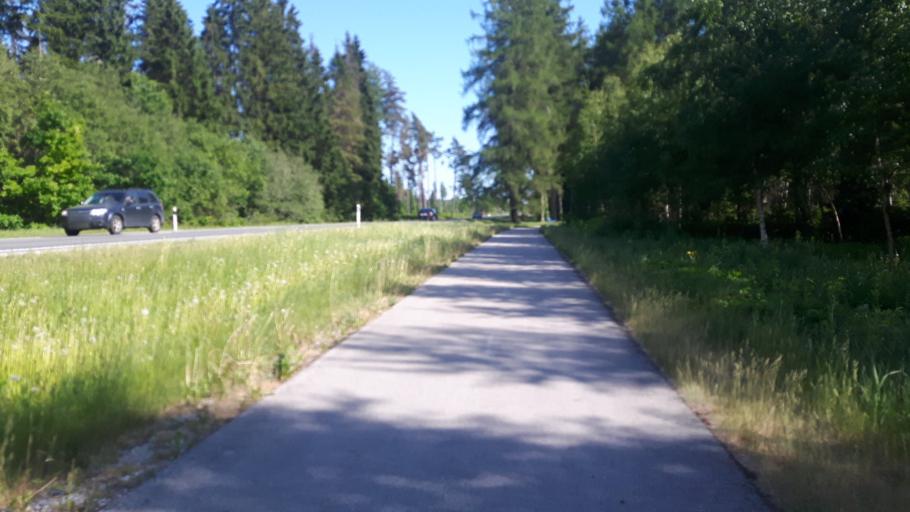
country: EE
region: Raplamaa
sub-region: Kehtna vald
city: Kehtna
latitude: 58.9608
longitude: 24.8620
